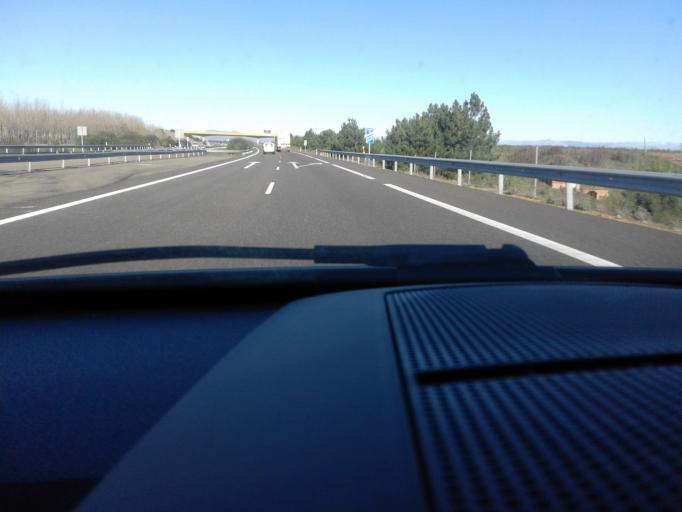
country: ES
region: Castille and Leon
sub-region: Provincia de Leon
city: Vega de Infanzones
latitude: 42.4804
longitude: -5.5515
